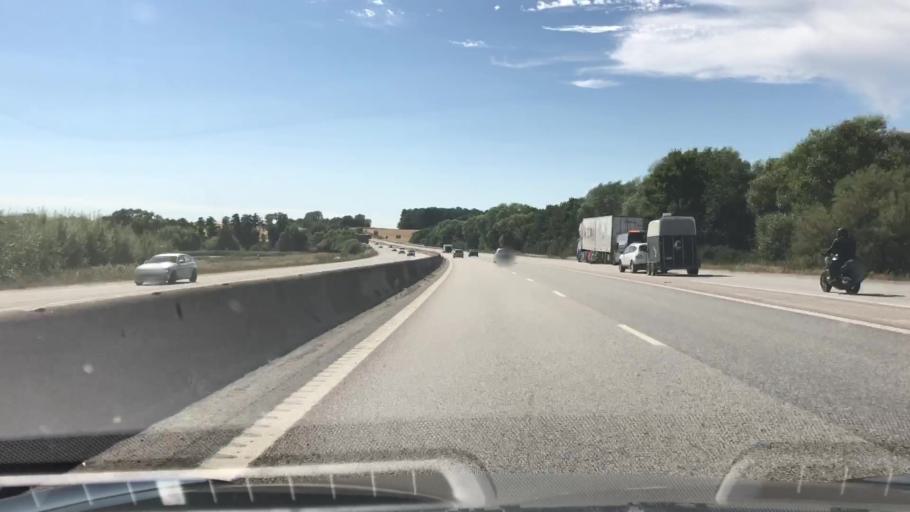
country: SE
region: Skane
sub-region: Eslovs Kommun
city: Eslov
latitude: 55.7701
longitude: 13.3117
